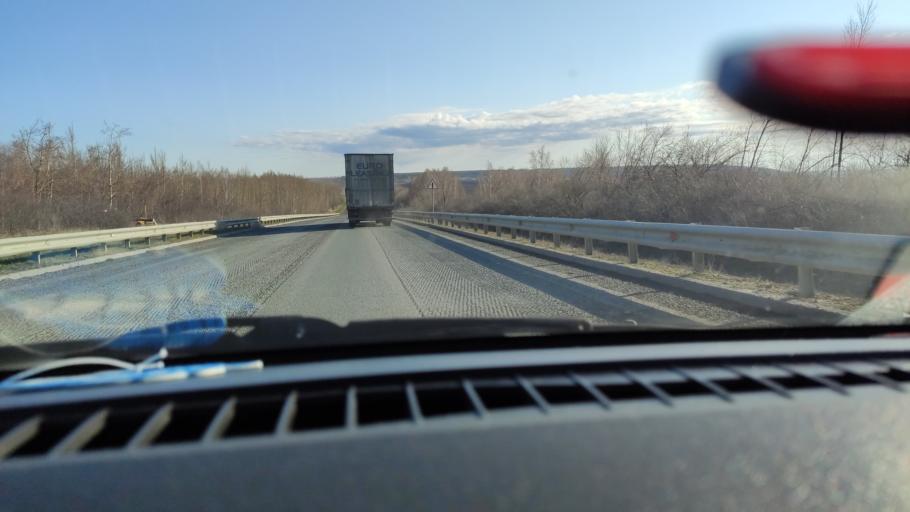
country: RU
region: Saratov
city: Dukhovnitskoye
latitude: 52.6900
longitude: 48.2425
